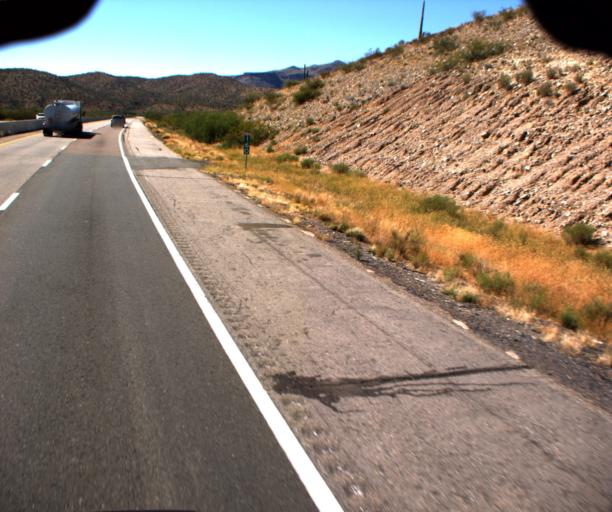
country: US
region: Arizona
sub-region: Yavapai County
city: Bagdad
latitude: 34.3781
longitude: -113.1922
